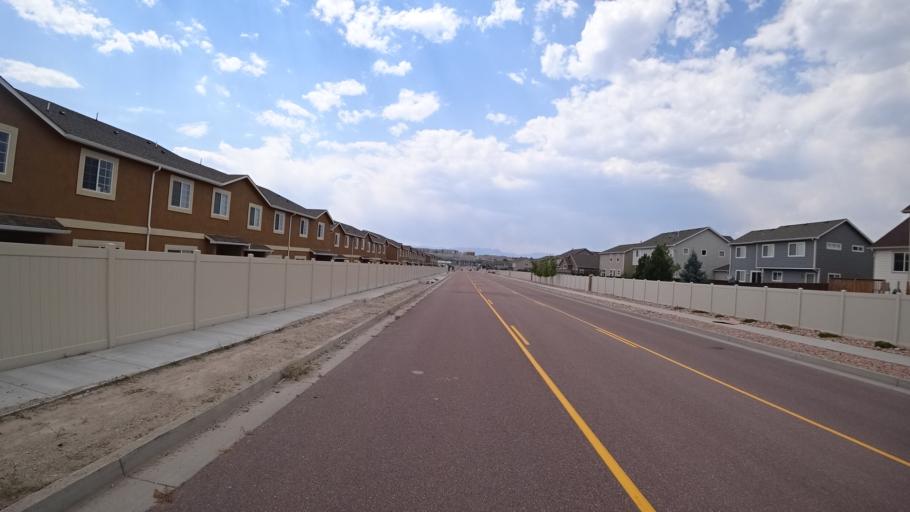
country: US
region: Colorado
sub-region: El Paso County
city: Black Forest
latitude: 38.9437
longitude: -104.6923
